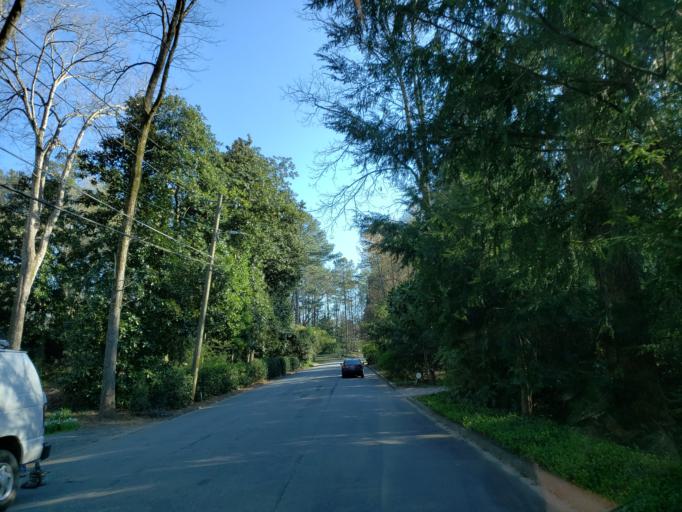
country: US
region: Georgia
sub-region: DeKalb County
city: North Atlanta
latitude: 33.8539
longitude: -84.3988
